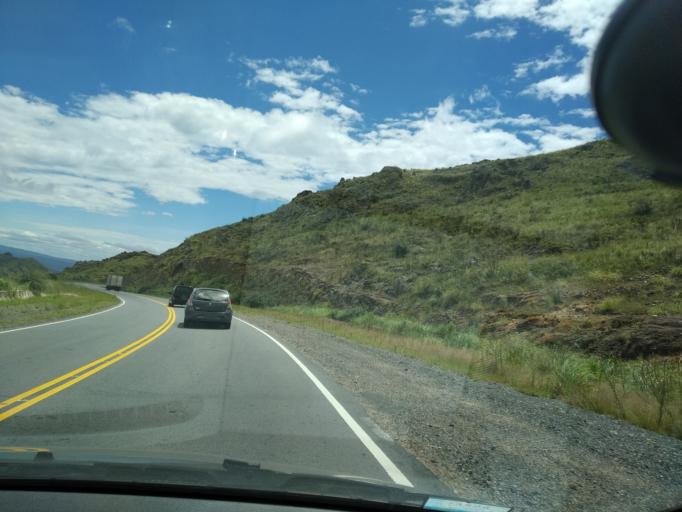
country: AR
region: Cordoba
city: Cuesta Blanca
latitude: -31.6044
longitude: -64.6993
